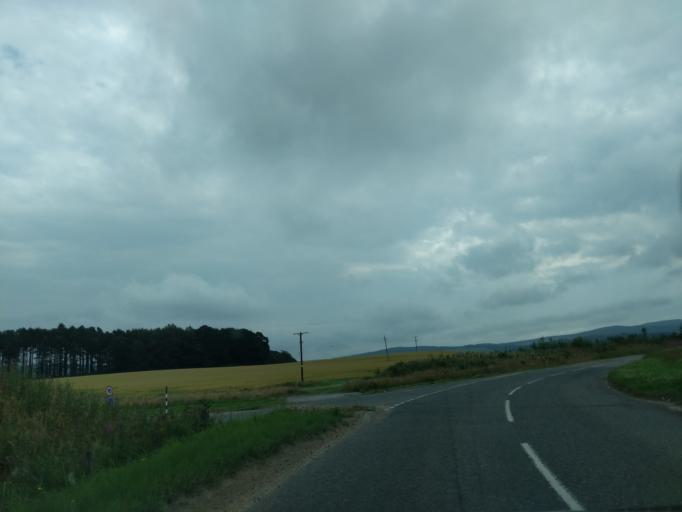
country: GB
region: Scotland
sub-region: Moray
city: Rothes
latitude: 57.4914
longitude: -3.2111
